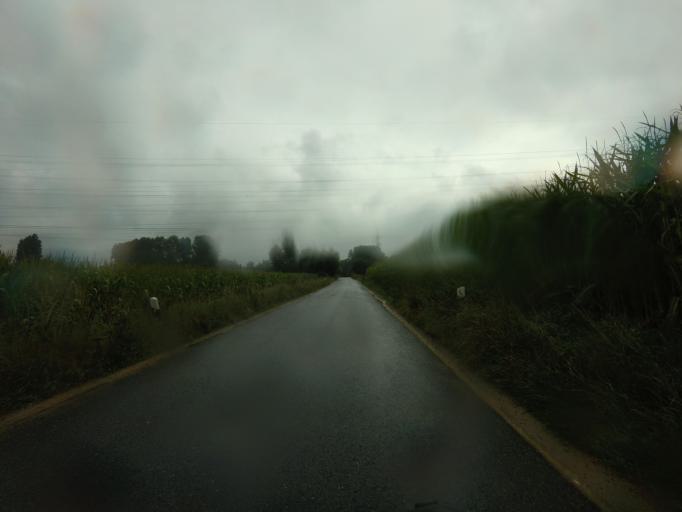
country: DE
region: North Rhine-Westphalia
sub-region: Regierungsbezirk Munster
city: Gronau
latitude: 52.1913
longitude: 7.0141
